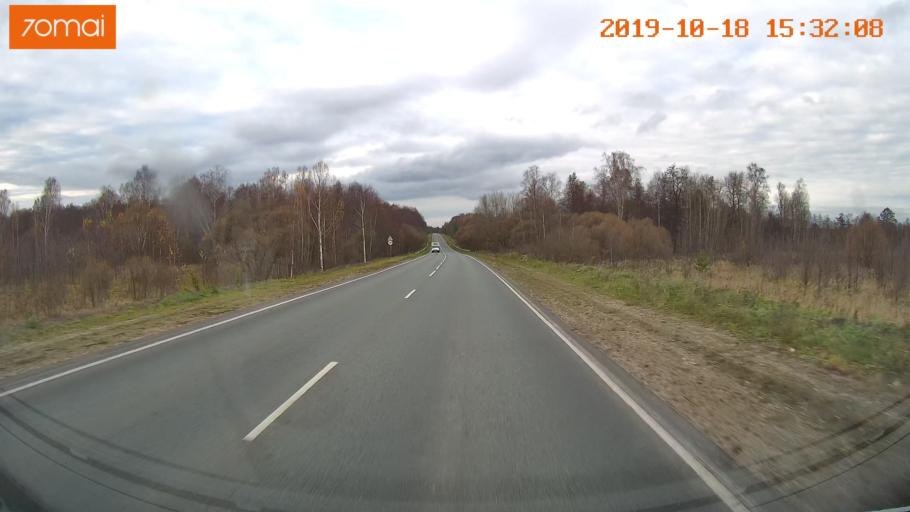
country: RU
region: Vladimir
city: Anopino
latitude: 55.8222
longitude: 40.6586
